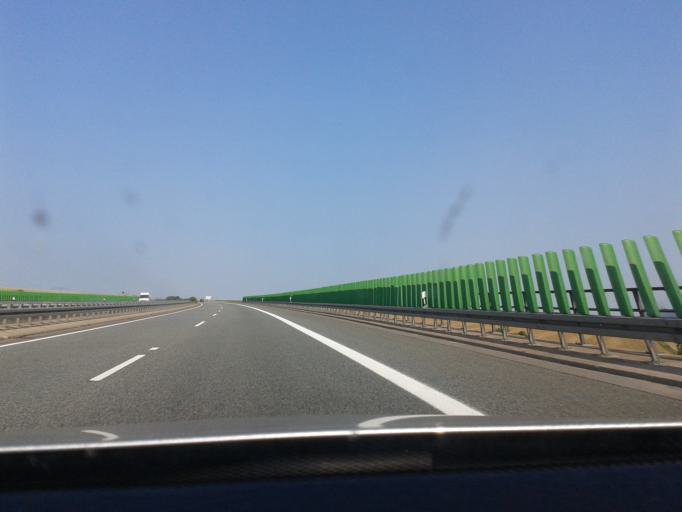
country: DE
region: Thuringia
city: Gorsbach
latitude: 51.4673
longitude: 10.9612
